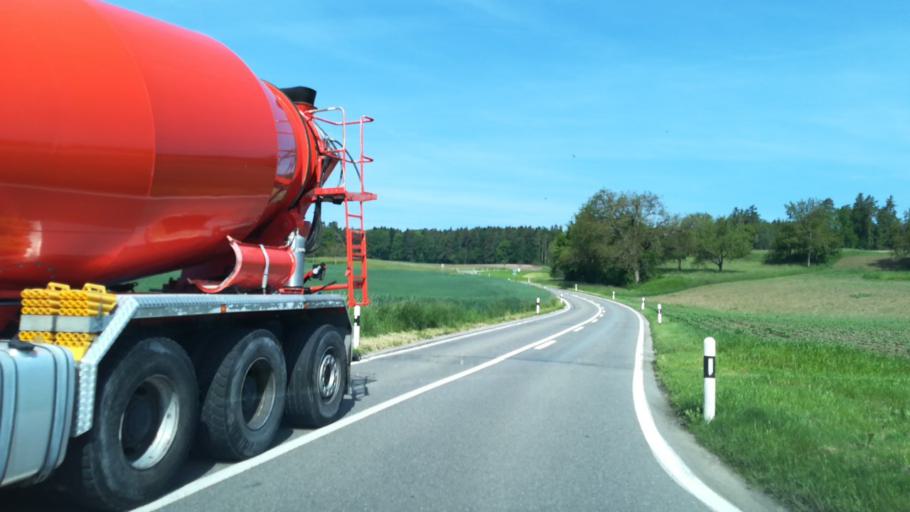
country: CH
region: Thurgau
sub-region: Frauenfeld District
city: Pfyn
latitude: 47.6037
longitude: 8.9458
